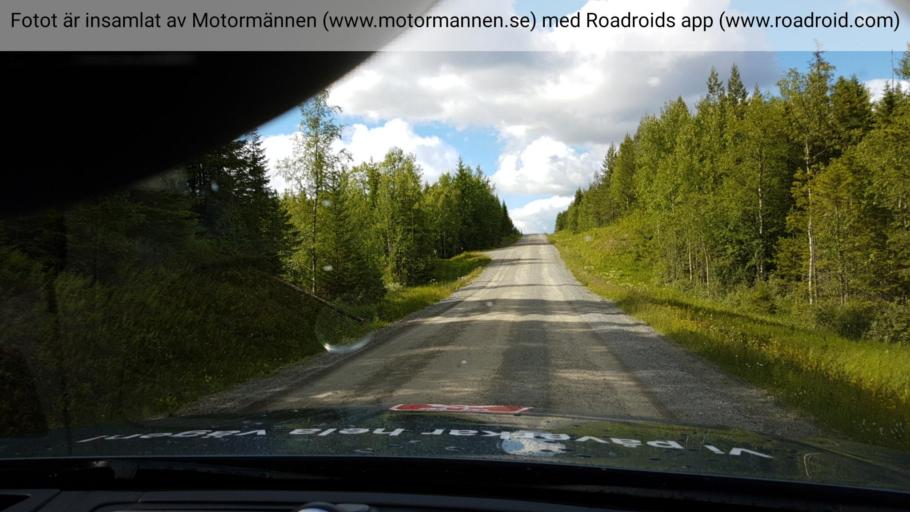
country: SE
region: Jaemtland
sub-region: Bergs Kommun
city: Hoverberg
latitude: 63.0226
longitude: 14.0831
